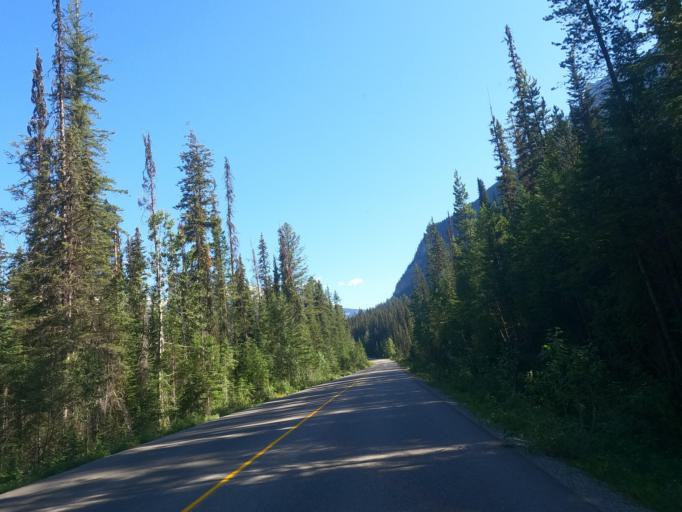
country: CA
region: Alberta
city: Lake Louise
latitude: 51.4086
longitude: -116.5355
